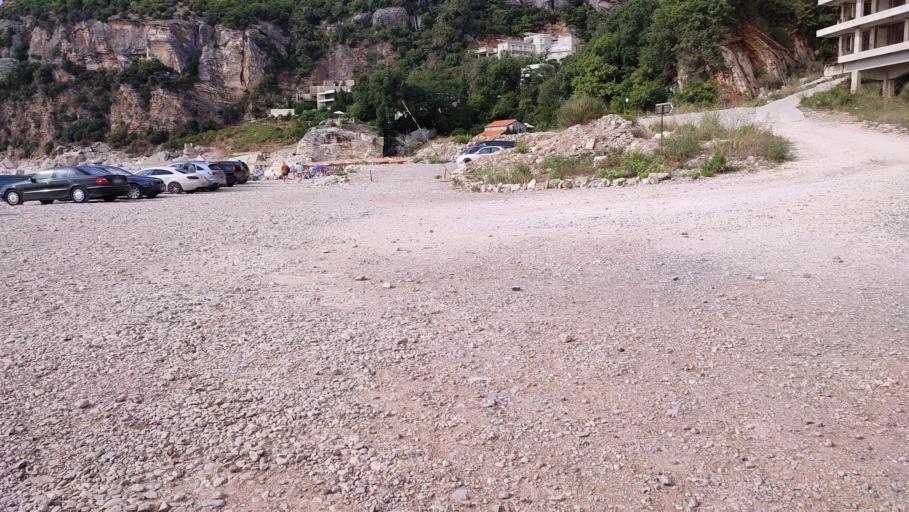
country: ME
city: Petrovac na Moru
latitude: 42.2106
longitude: 18.9258
